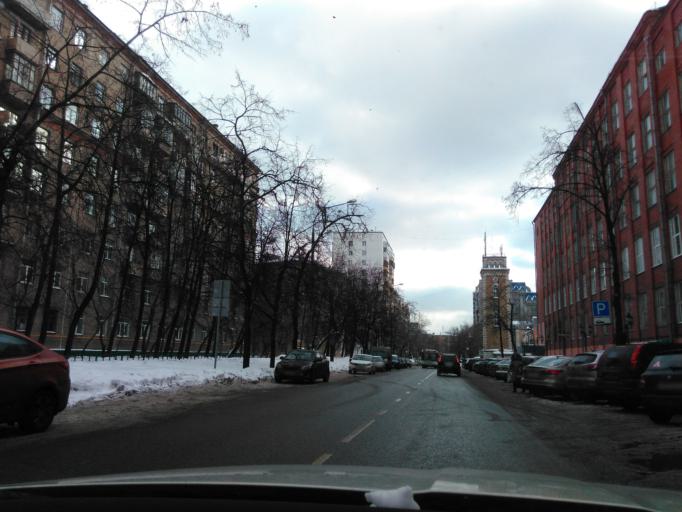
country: RU
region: Moscow
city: Sokol
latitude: 55.8010
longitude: 37.5652
